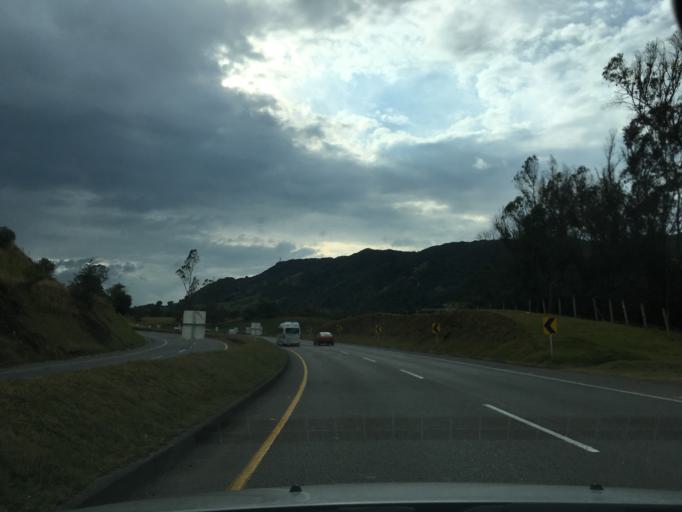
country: CO
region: Boyaca
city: Ventaquemada
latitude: 5.3974
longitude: -73.4926
